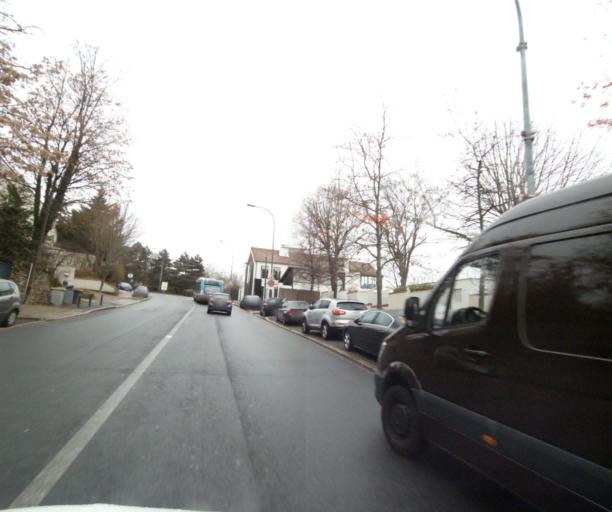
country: FR
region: Ile-de-France
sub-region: Departement des Hauts-de-Seine
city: Suresnes
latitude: 48.8750
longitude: 2.2201
